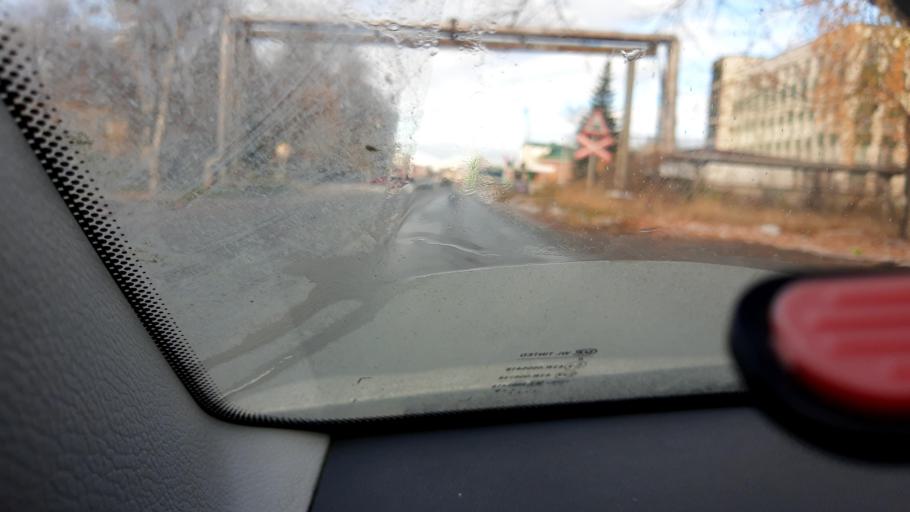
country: RU
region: Bashkortostan
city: Ufa
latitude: 54.8032
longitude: 56.0997
